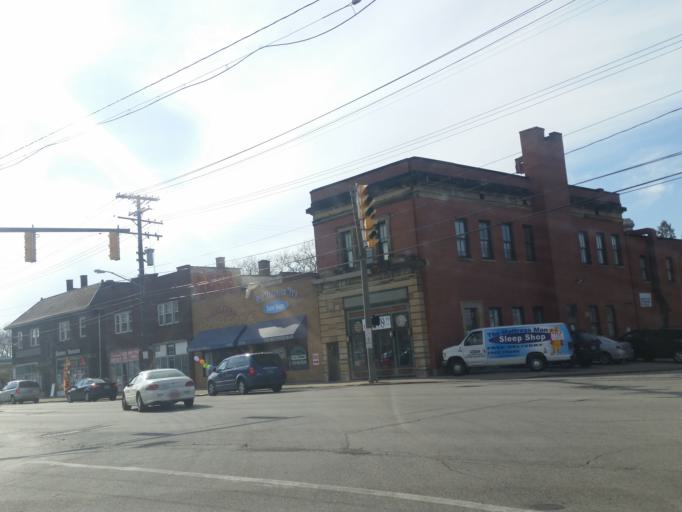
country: US
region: Ohio
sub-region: Cuyahoga County
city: Brooklyn
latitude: 41.4666
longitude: -81.7540
